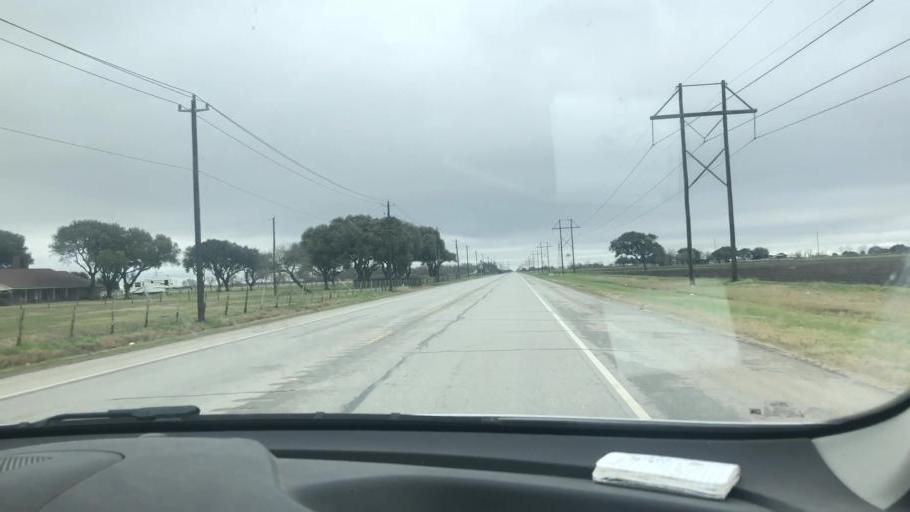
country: US
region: Texas
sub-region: Wharton County
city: Boling
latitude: 29.2039
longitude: -96.0224
